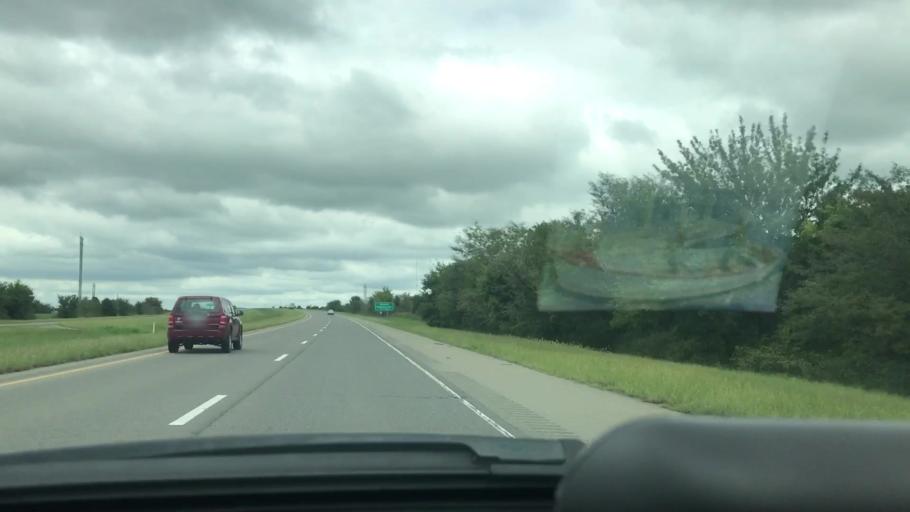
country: US
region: Oklahoma
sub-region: McIntosh County
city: Checotah
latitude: 35.5675
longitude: -95.4915
